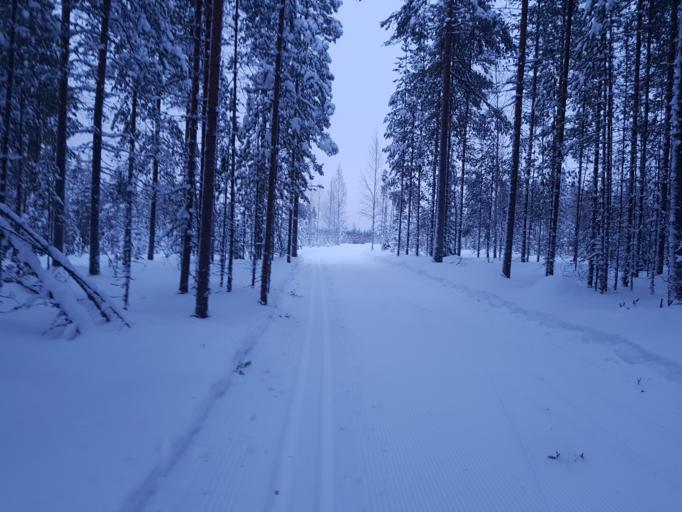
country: FI
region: Kainuu
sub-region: Kehys-Kainuu
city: Kuhmo
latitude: 64.0875
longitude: 29.5149
